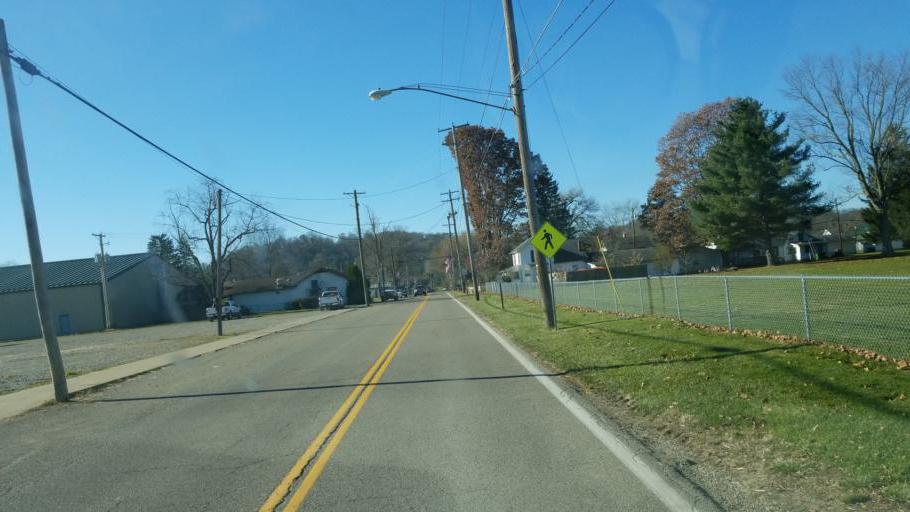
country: US
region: Ohio
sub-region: Muskingum County
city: Dresden
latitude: 40.1195
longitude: -82.0064
